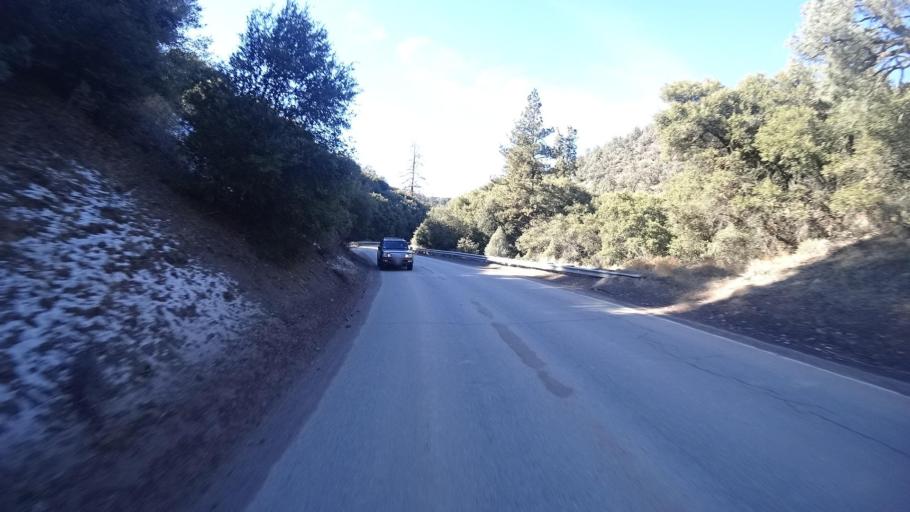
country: US
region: California
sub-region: Kern County
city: Pine Mountain Club
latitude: 34.8530
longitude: -119.1261
